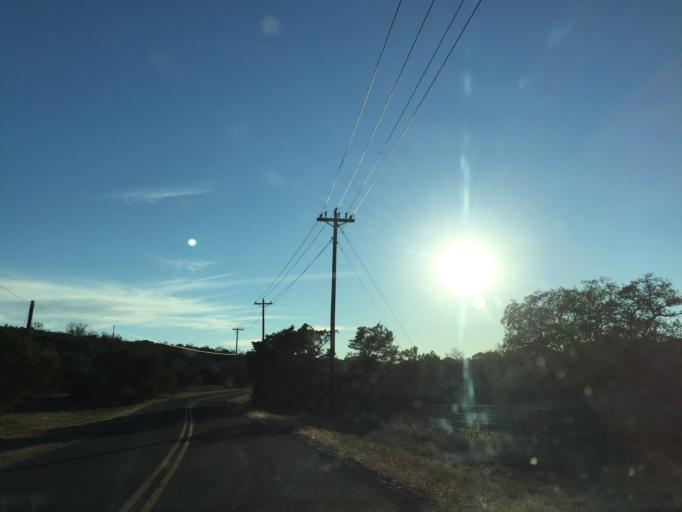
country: US
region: Texas
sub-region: Travis County
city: Lago Vista
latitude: 30.5038
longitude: -98.0538
